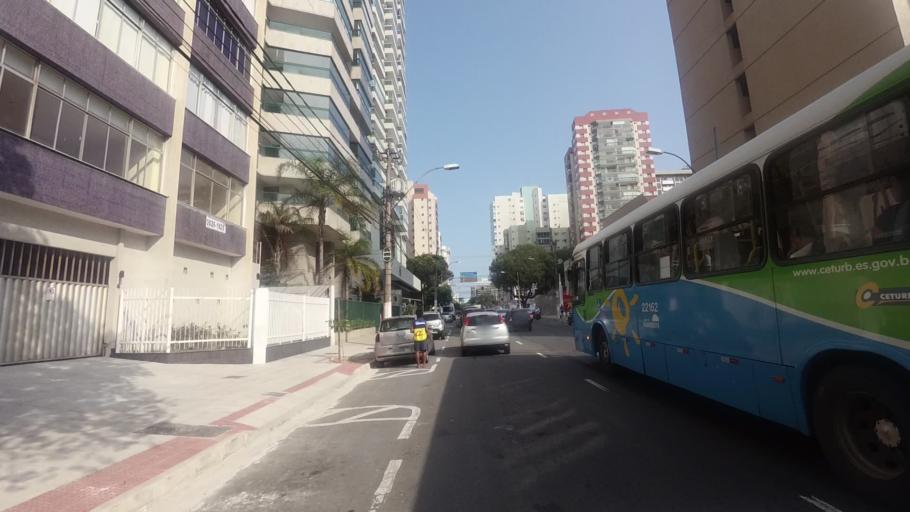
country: BR
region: Espirito Santo
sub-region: Vila Velha
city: Vila Velha
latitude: -20.3073
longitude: -40.2935
